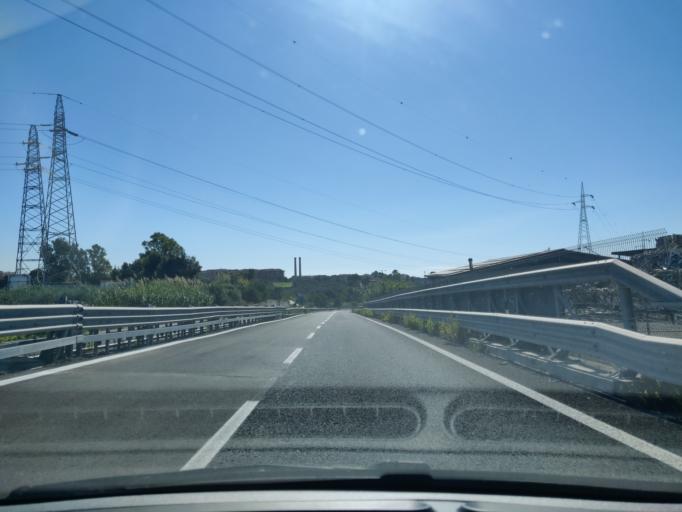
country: IT
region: Latium
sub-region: Citta metropolitana di Roma Capitale
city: Civitavecchia
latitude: 42.1107
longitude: 11.7925
